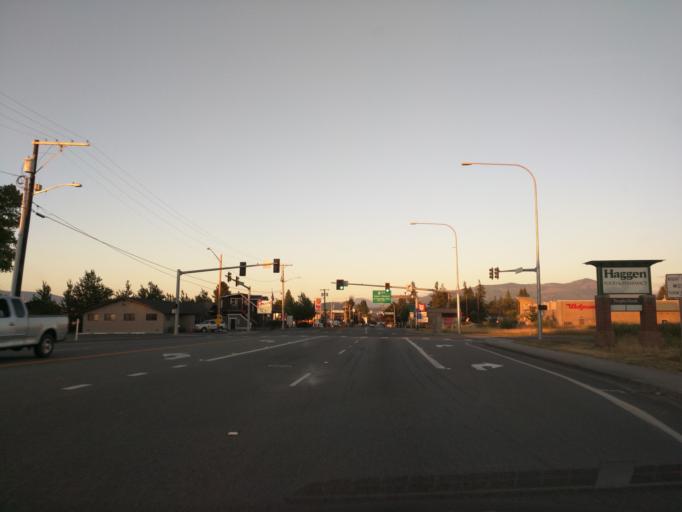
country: US
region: Washington
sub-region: Skagit County
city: Burlington
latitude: 48.4717
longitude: -122.3388
